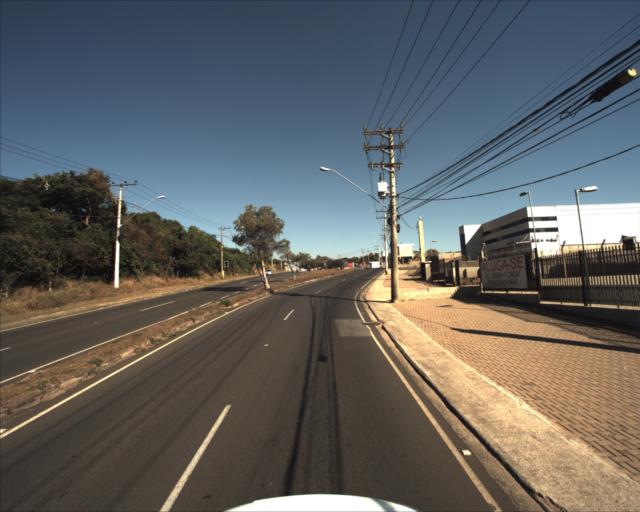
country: BR
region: Sao Paulo
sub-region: Sorocaba
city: Sorocaba
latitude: -23.4530
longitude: -47.4183
